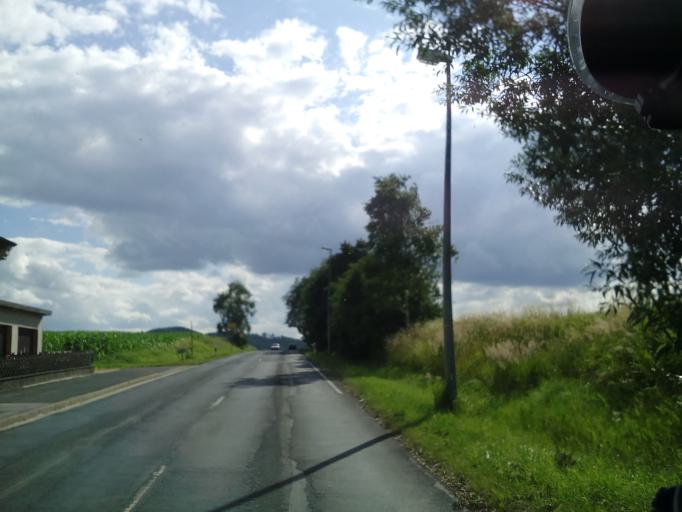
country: DE
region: Bavaria
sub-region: Upper Franconia
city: Neustadt bei Coburg
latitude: 50.3169
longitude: 11.0990
